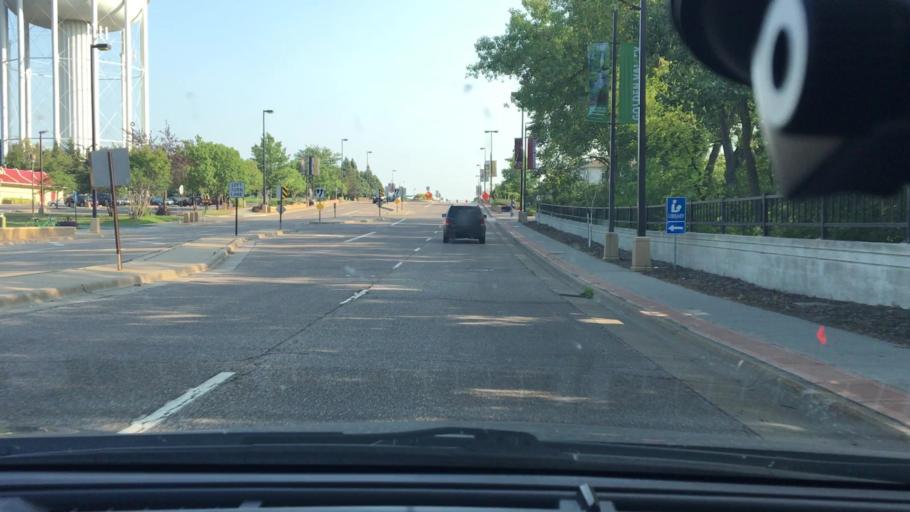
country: US
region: Minnesota
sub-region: Hennepin County
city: Golden Valley
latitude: 44.9885
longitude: -93.3805
